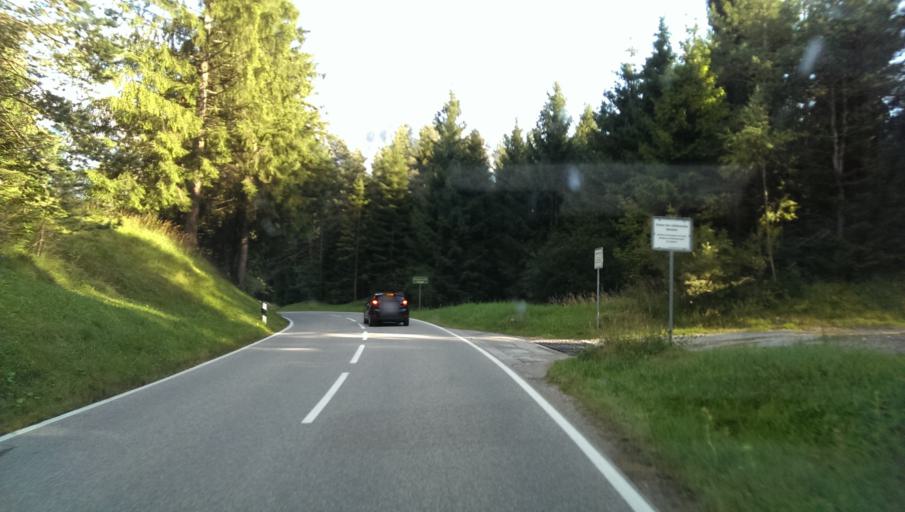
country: DE
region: Bavaria
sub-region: Upper Bavaria
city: Mittenwald
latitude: 47.4691
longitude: 11.2577
